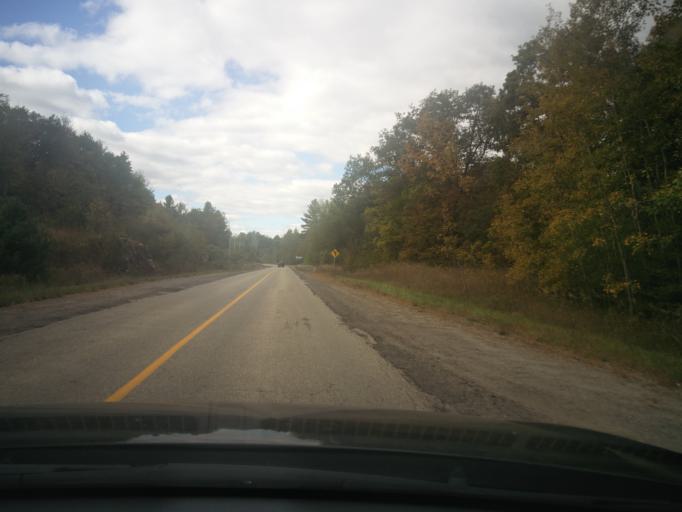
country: CA
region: Ontario
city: Perth
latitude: 44.6409
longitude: -76.5308
